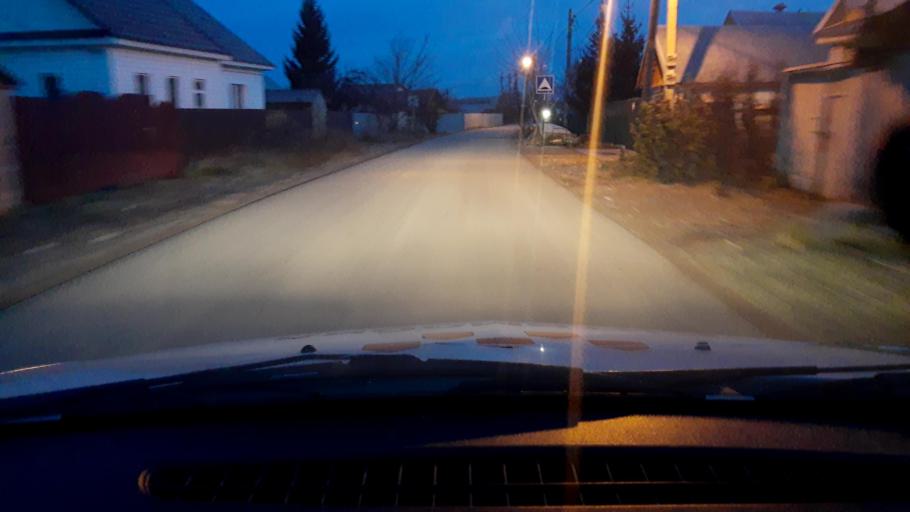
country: RU
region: Bashkortostan
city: Iglino
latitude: 54.7774
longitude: 56.2172
